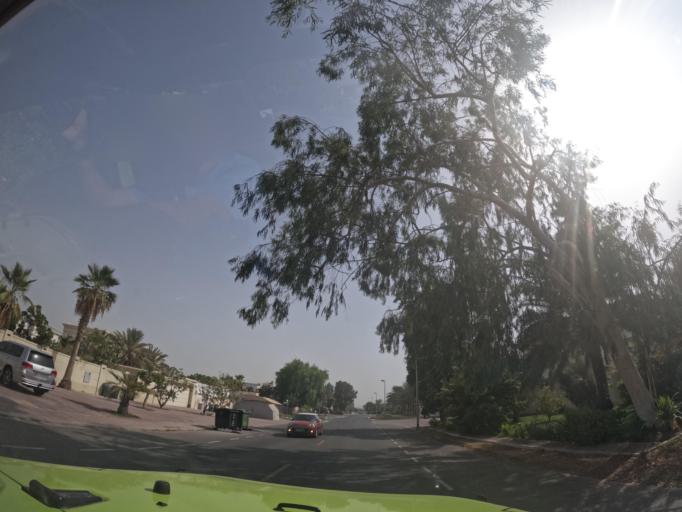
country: AE
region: Dubai
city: Dubai
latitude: 25.1424
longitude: 55.2102
